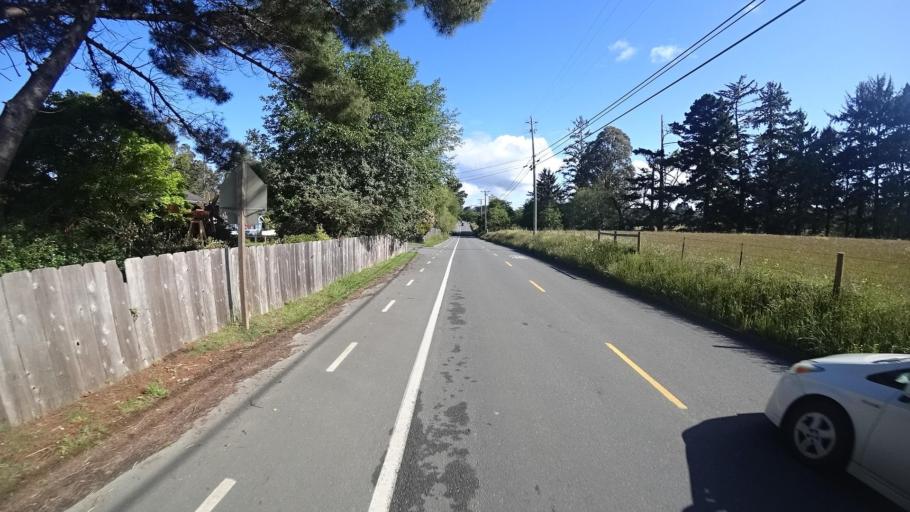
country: US
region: California
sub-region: Humboldt County
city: McKinleyville
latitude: 40.9574
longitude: -124.1104
